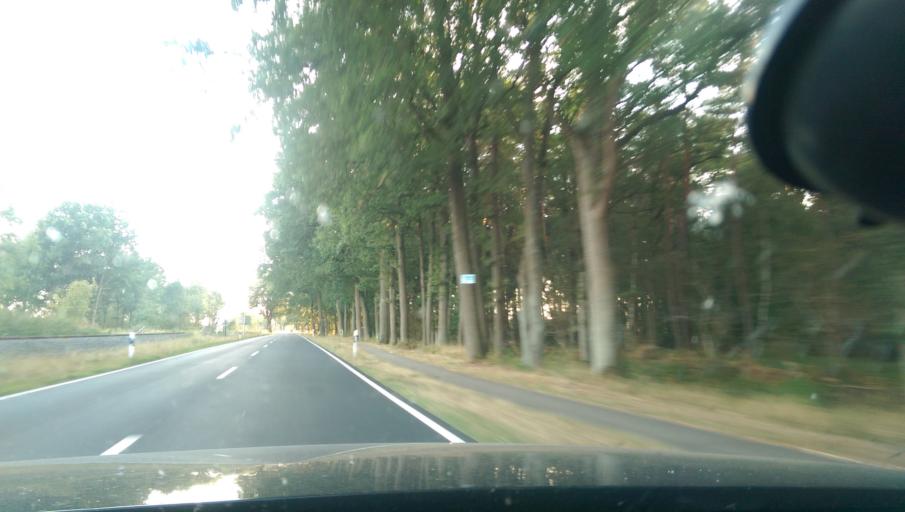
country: DE
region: Lower Saxony
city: Walsrode
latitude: 52.8093
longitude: 9.5934
